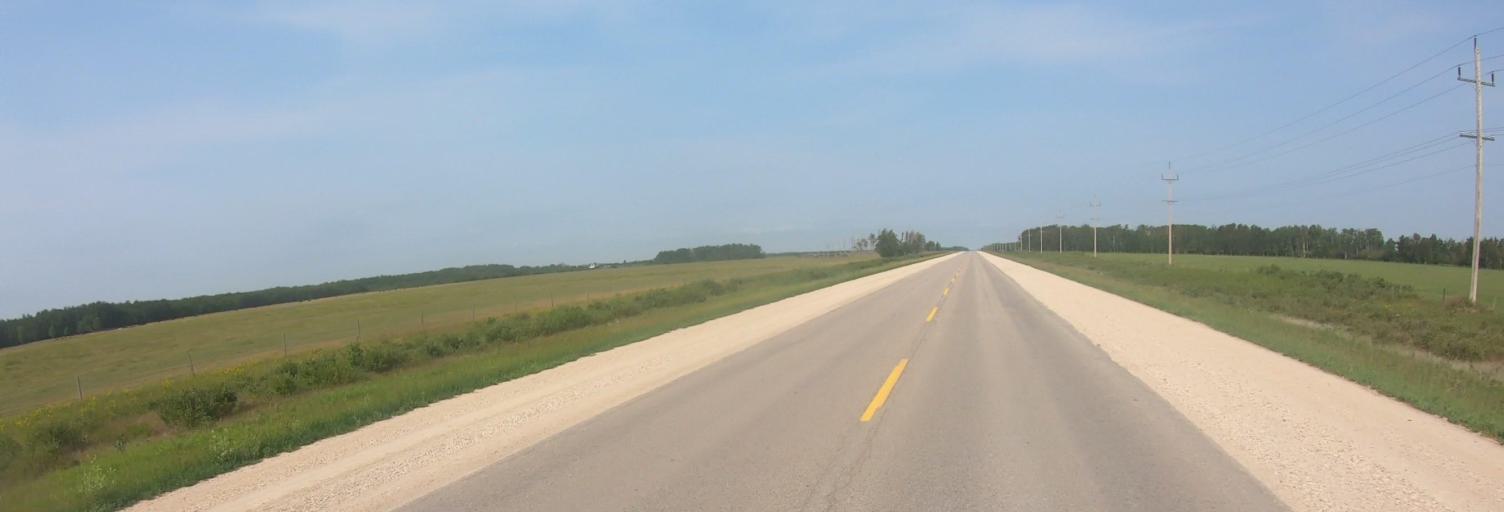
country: CA
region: Manitoba
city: La Broquerie
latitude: 49.3080
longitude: -96.5610
